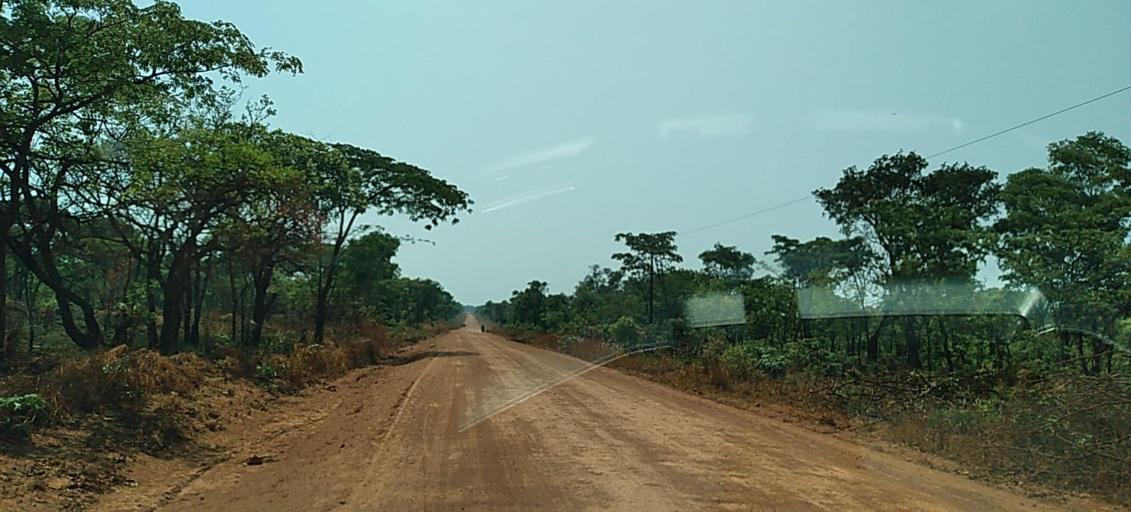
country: ZM
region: North-Western
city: Kansanshi
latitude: -11.9929
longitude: 26.6266
